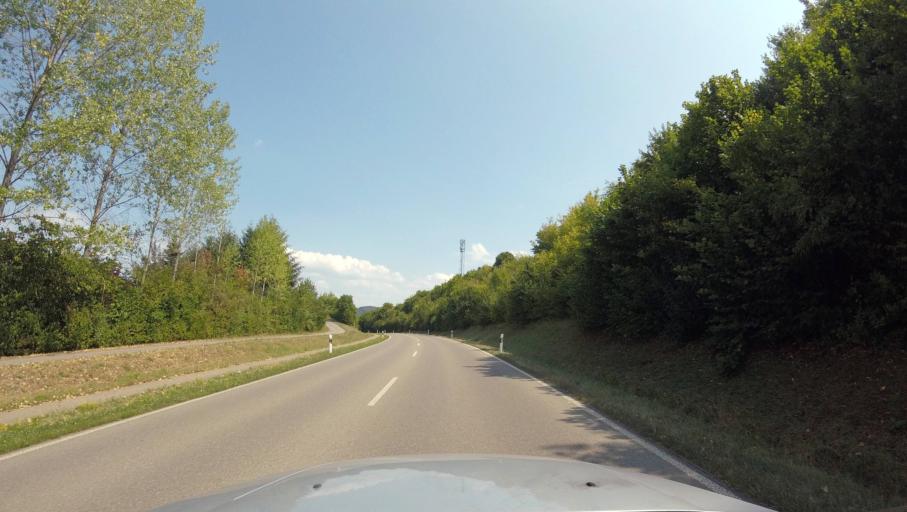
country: DE
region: Baden-Wuerttemberg
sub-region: Regierungsbezirk Stuttgart
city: Oppenweiler
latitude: 48.9526
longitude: 9.4902
